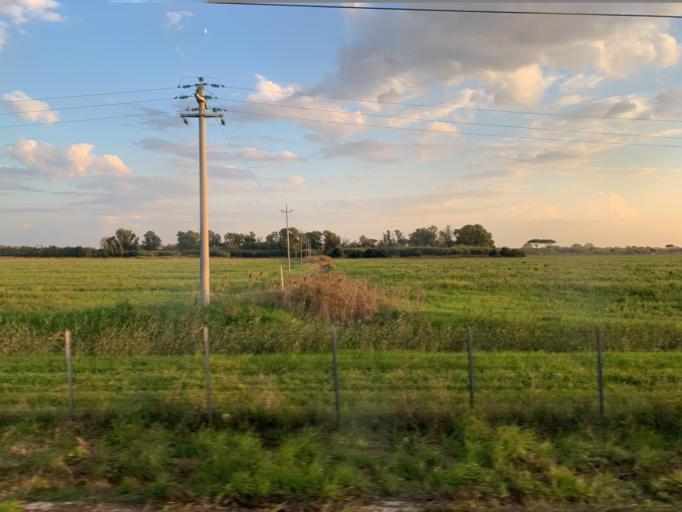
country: IT
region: Latium
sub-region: Citta metropolitana di Roma Capitale
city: Npp 23 (Parco Leonardo)
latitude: 41.7925
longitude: 12.2799
